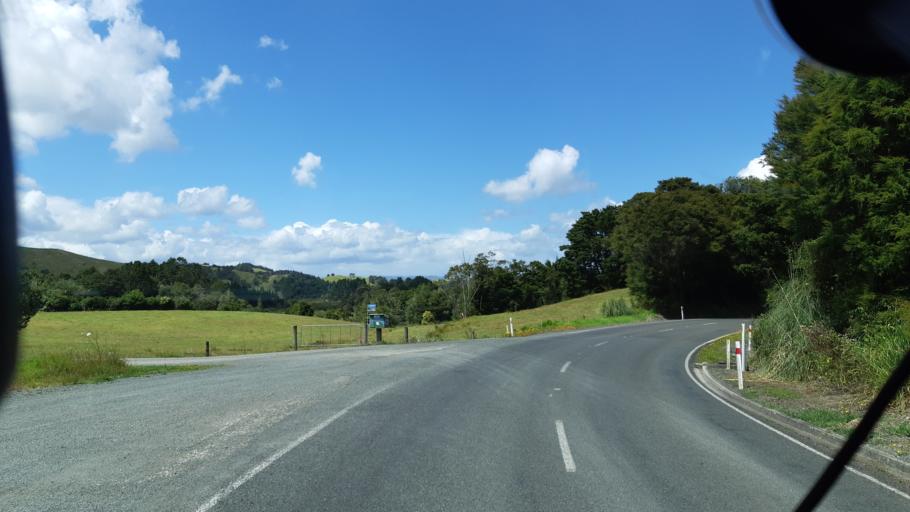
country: NZ
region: Northland
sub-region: Far North District
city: Taipa
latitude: -35.2559
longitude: 173.5343
